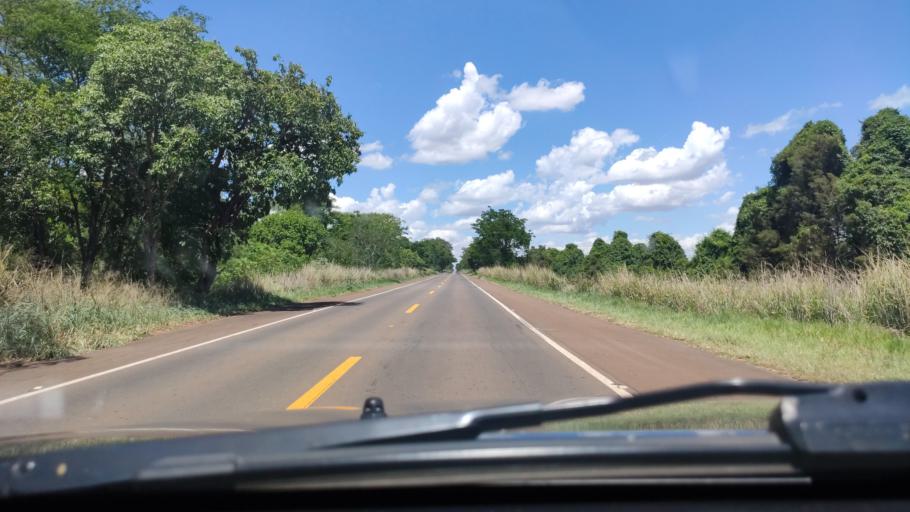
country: BR
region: Sao Paulo
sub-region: Boa Esperanca Do Sul
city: Boa Esperanca do Sul
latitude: -22.0692
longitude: -48.3854
